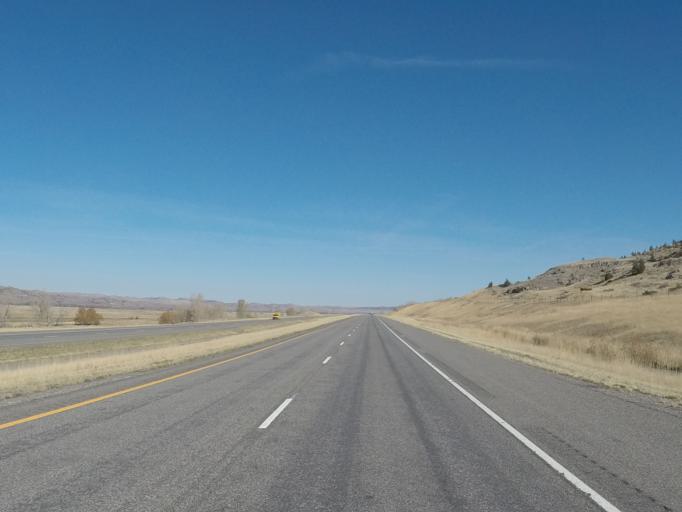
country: US
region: Montana
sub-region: Sweet Grass County
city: Big Timber
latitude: 45.7934
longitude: -110.0391
